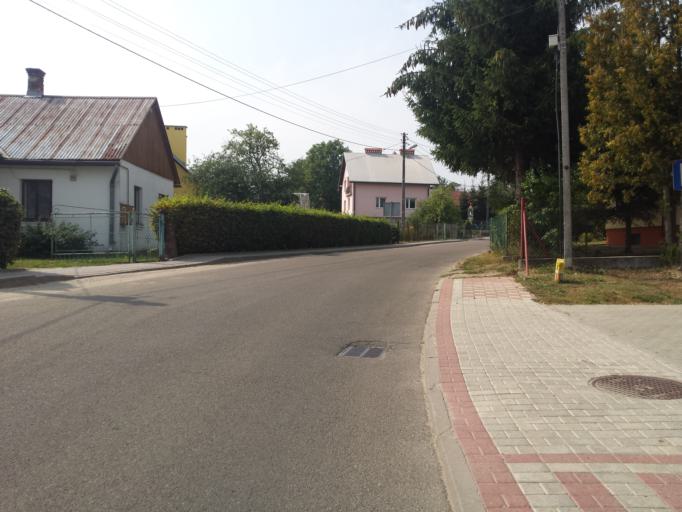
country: PL
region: Subcarpathian Voivodeship
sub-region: Powiat rzeszowski
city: Dynow
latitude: 49.8184
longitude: 22.2173
